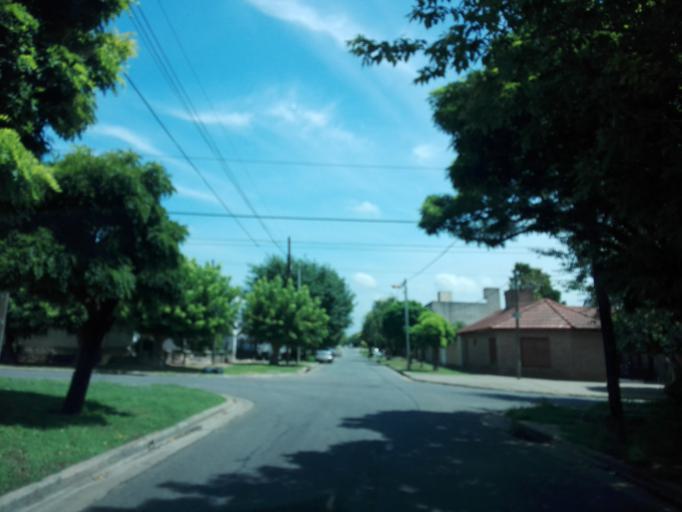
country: AR
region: Buenos Aires
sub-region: Partido de La Plata
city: La Plata
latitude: -34.9505
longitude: -57.9759
